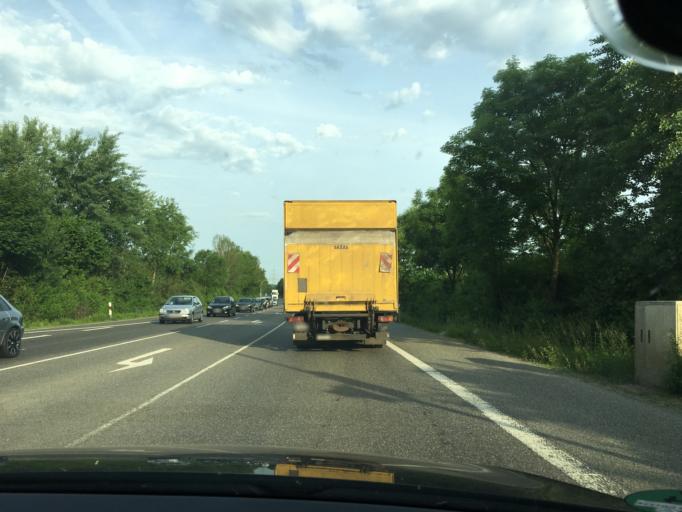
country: DE
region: North Rhine-Westphalia
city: Julich
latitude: 50.9121
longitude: 6.3499
